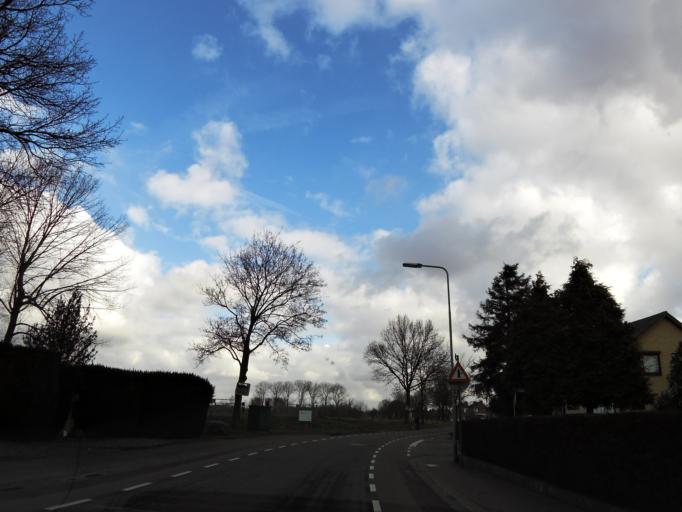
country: NL
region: Limburg
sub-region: Gemeente Stein
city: Berg
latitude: 51.0113
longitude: 5.7736
